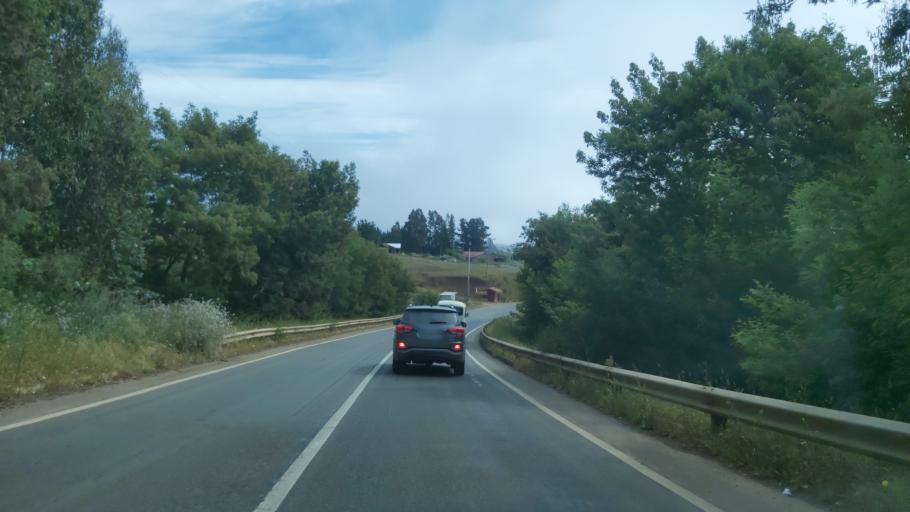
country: CL
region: Maule
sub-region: Provincia de Cauquenes
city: Cauquenes
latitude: -35.8695
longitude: -72.6552
